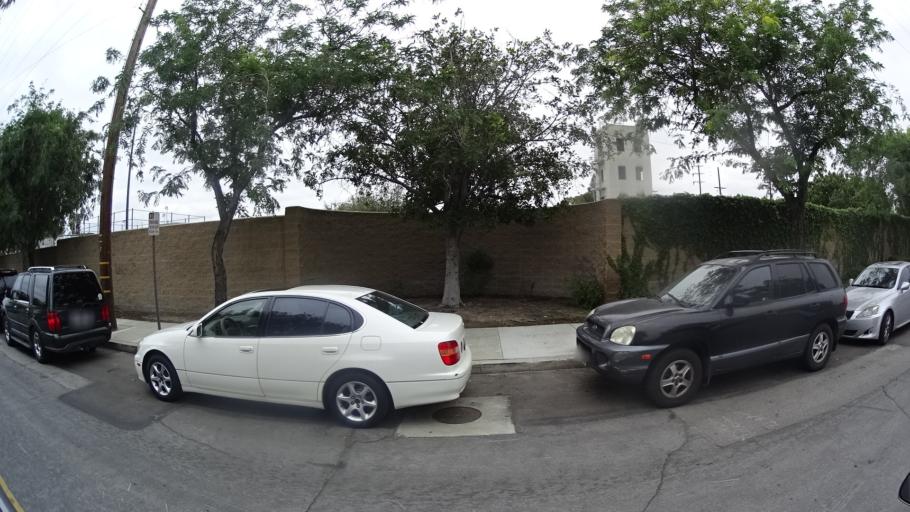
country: US
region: California
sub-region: Los Angeles County
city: Burbank
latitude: 34.1877
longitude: -118.3447
